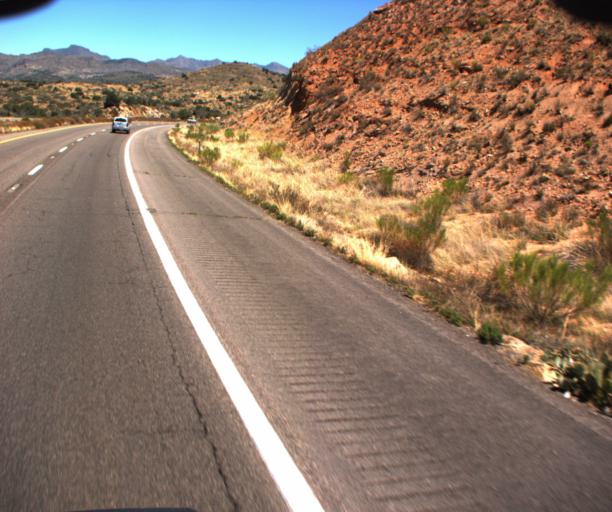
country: US
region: Arizona
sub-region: Gila County
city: Tonto Basin
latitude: 33.8578
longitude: -111.4736
